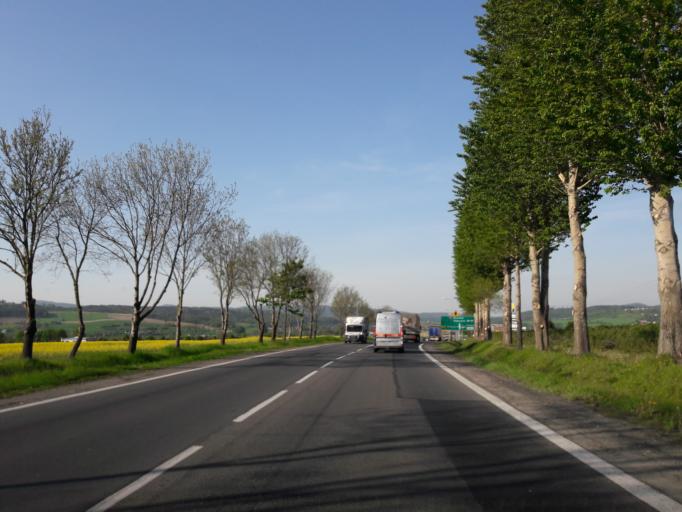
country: PL
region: Lower Silesian Voivodeship
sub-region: Powiat klodzki
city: Klodzko
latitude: 50.4506
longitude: 16.6317
